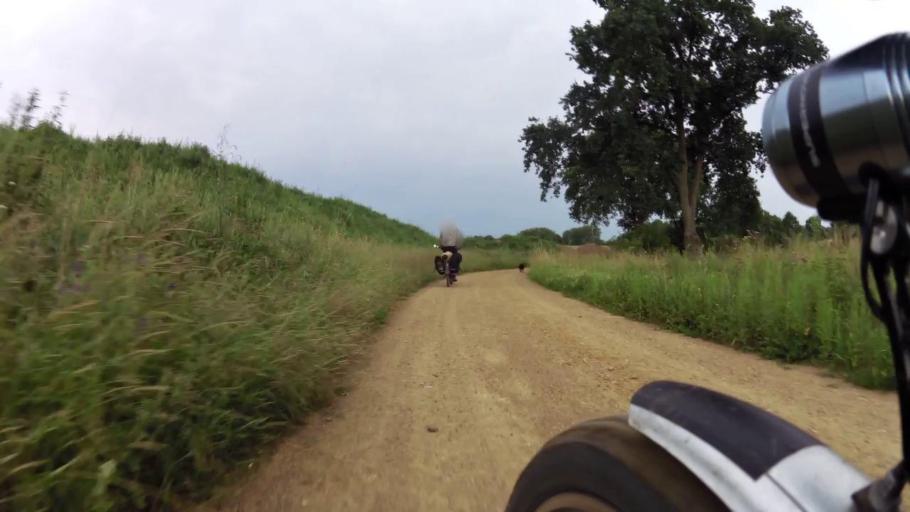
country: PL
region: West Pomeranian Voivodeship
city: Trzcinsko Zdroj
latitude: 52.8770
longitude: 14.6001
